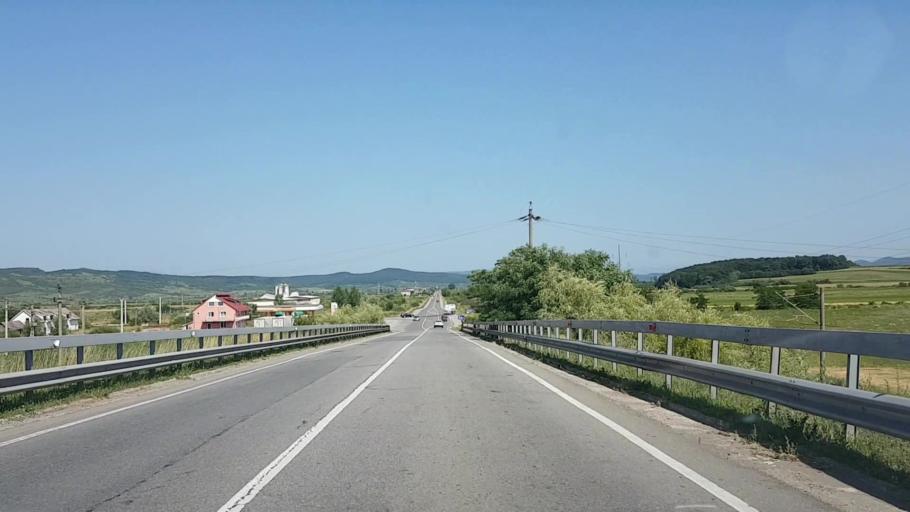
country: RO
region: Bistrita-Nasaud
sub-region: Comuna Sintereag
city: Cociu
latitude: 47.1826
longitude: 24.2355
